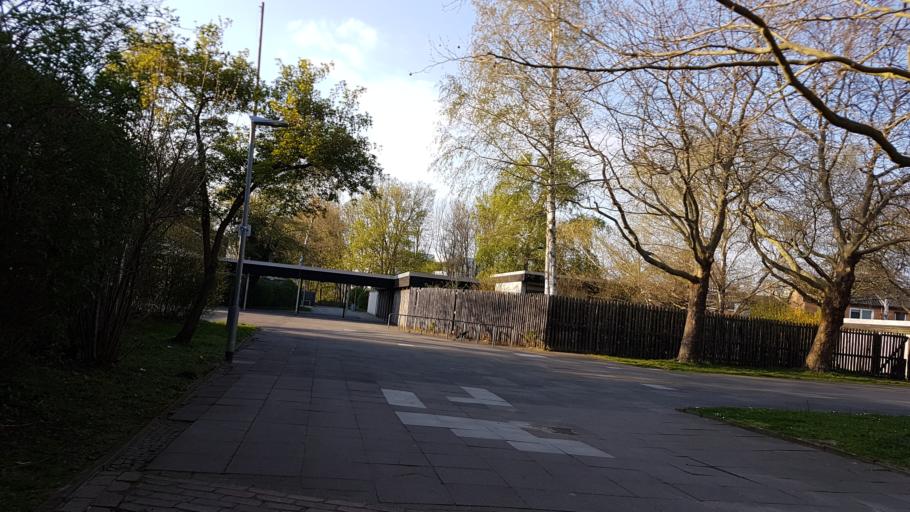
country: DE
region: Lower Saxony
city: Ronnenberg
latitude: 52.3440
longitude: 9.6837
